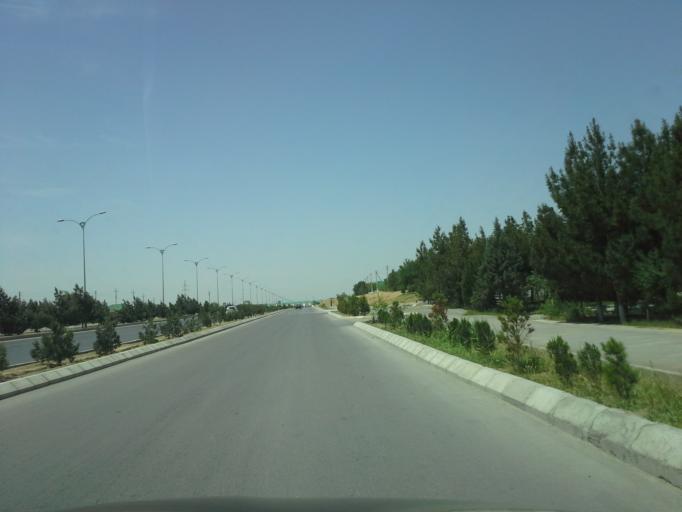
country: TM
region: Ahal
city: Ashgabat
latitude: 37.9991
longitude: 58.4074
